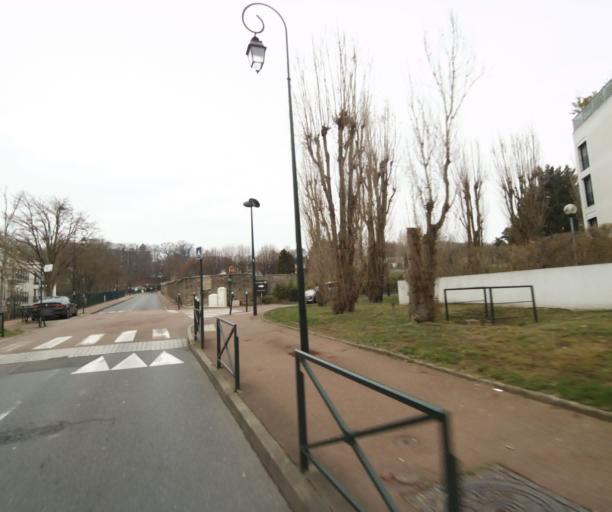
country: FR
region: Ile-de-France
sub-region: Departement des Hauts-de-Seine
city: Vaucresson
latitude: 48.8391
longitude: 2.1645
